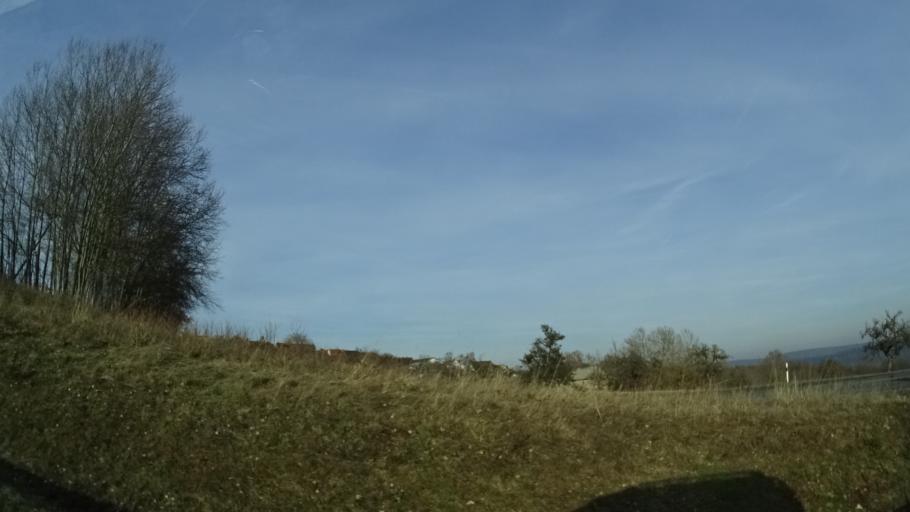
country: DE
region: Bavaria
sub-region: Regierungsbezirk Unterfranken
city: Sandberg
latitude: 50.3245
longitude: 9.9805
